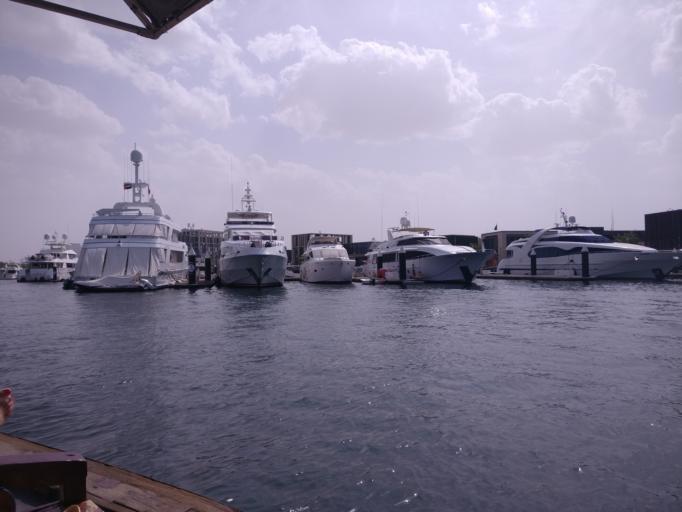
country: AE
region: Ash Shariqah
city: Sharjah
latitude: 25.2602
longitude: 55.3110
